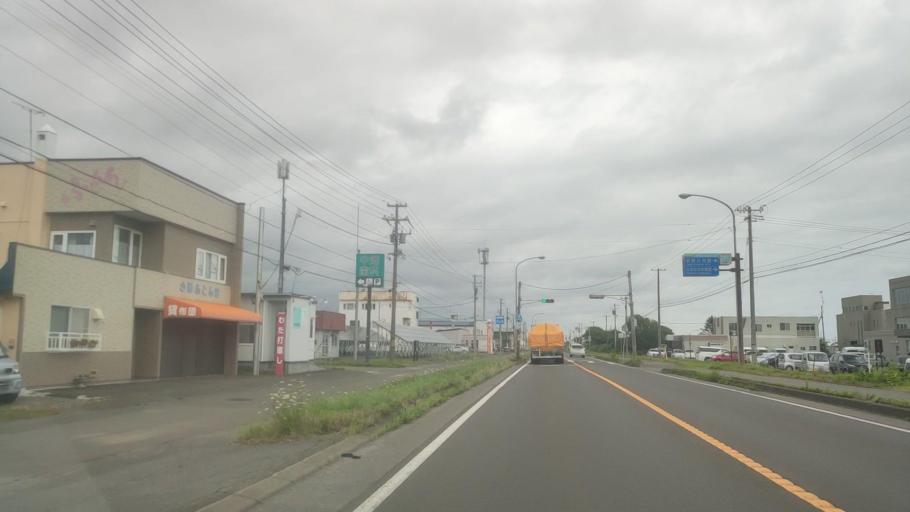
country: JP
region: Hokkaido
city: Shiraoi
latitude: 42.5162
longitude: 141.3004
